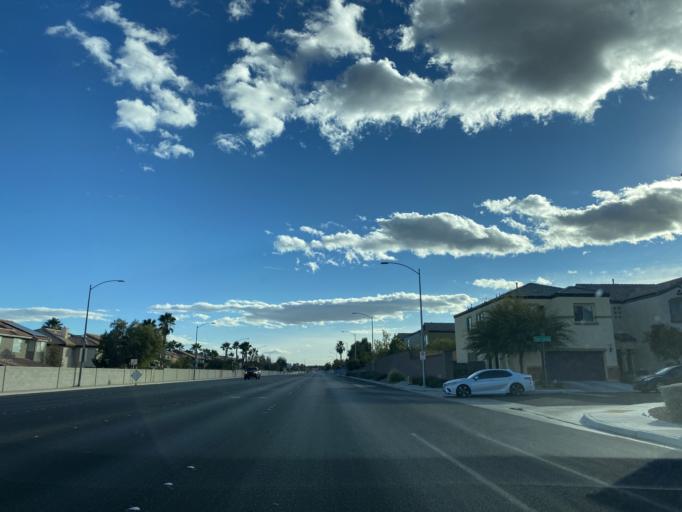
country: US
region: Nevada
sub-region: Clark County
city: Summerlin South
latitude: 36.2294
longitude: -115.2976
